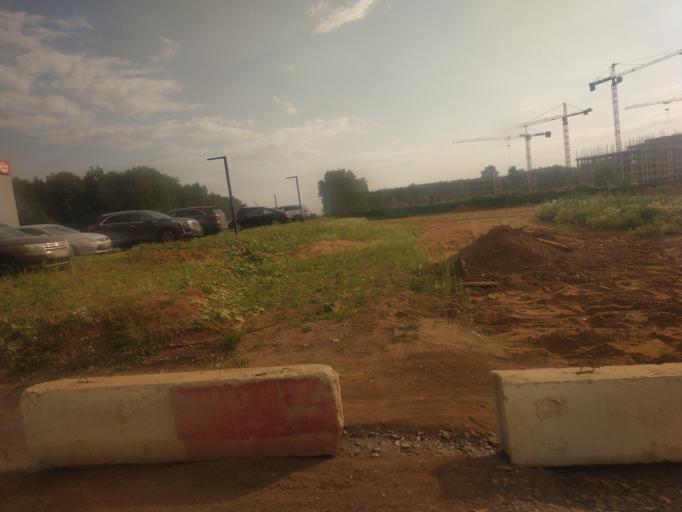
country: RU
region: Moskovskaya
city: Mosrentgen
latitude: 55.5898
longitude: 37.4518
